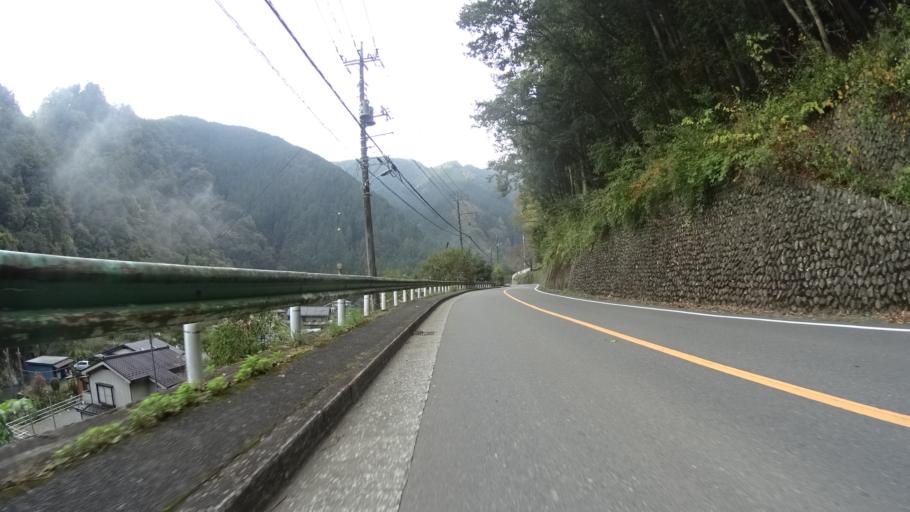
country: JP
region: Tokyo
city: Itsukaichi
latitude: 35.7039
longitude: 139.1429
